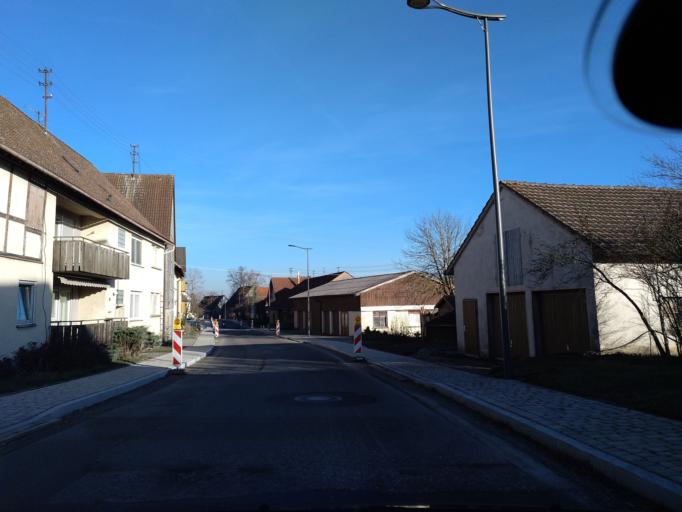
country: DE
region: Baden-Wuerttemberg
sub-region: Regierungsbezirk Stuttgart
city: Rosenberg
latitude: 49.0706
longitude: 10.0307
